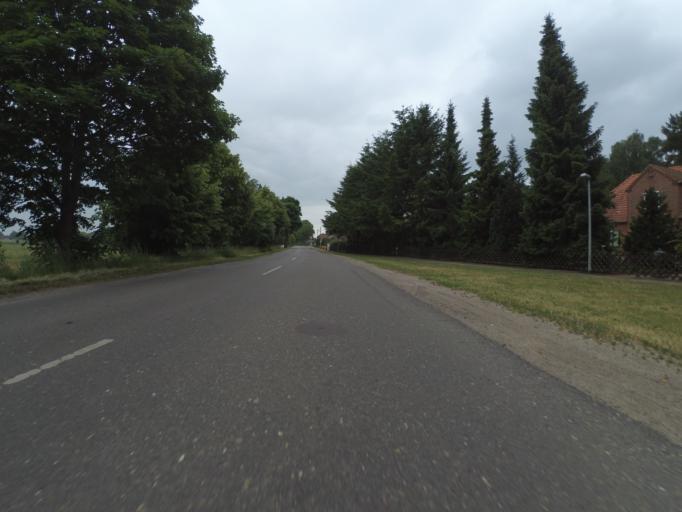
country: DE
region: Mecklenburg-Vorpommern
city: Neustadt-Glewe
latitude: 53.3671
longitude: 11.6575
